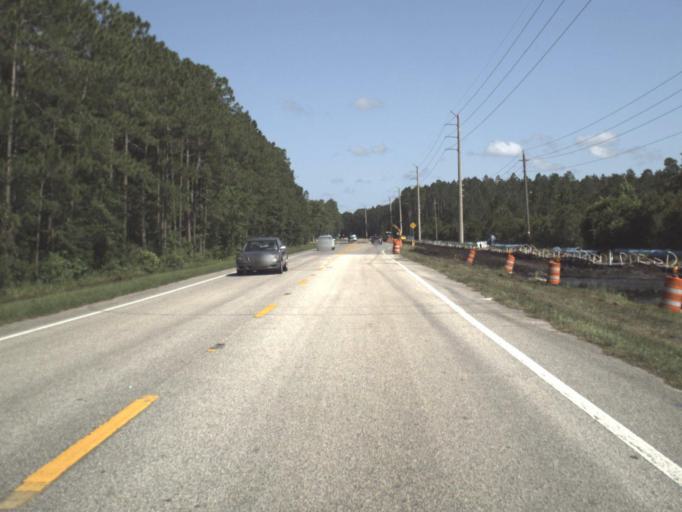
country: US
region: Florida
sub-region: Saint Johns County
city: Saint Augustine
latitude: 29.9402
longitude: -81.4386
